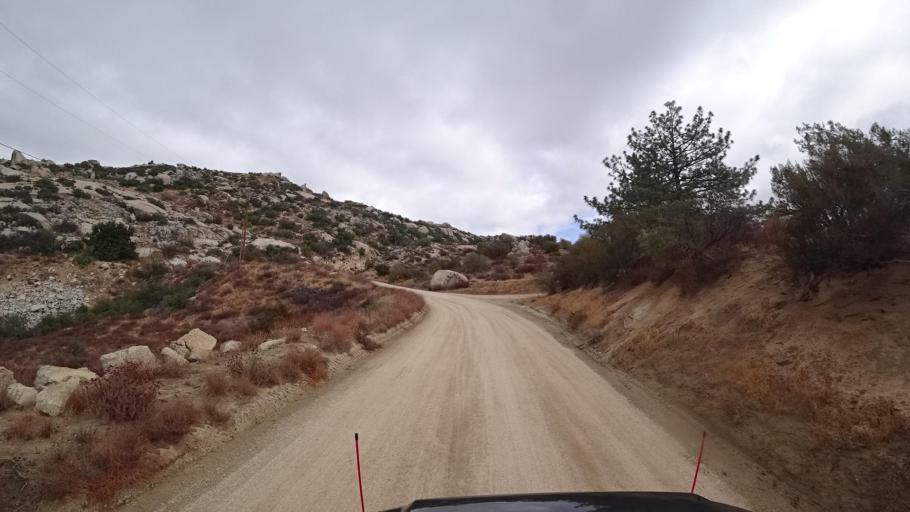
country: US
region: California
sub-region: San Diego County
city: Campo
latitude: 32.7096
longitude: -116.3862
